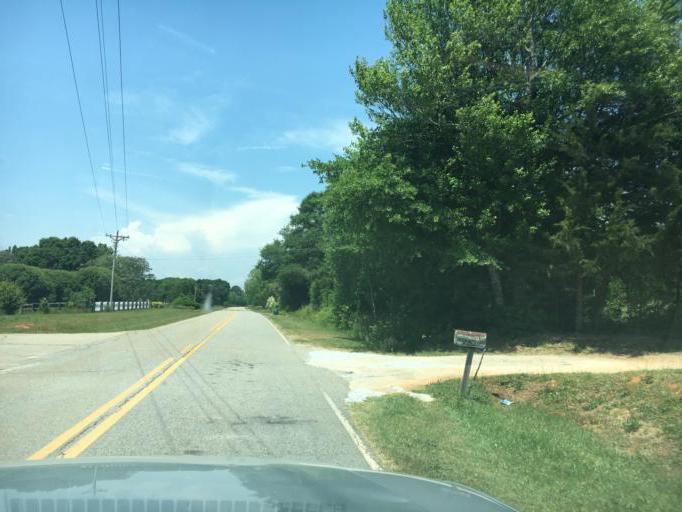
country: US
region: Georgia
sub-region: Hart County
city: Royston
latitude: 34.2998
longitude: -83.0903
